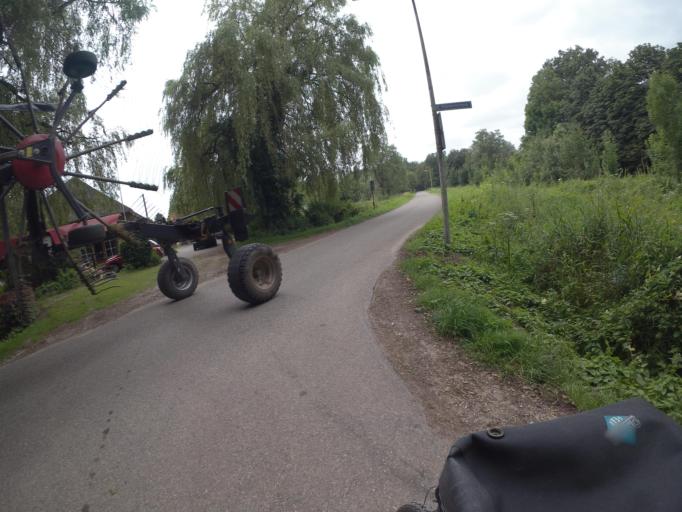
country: NL
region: Gelderland
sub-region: Gemeente Brummen
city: Brummen
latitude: 52.0776
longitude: 6.1359
